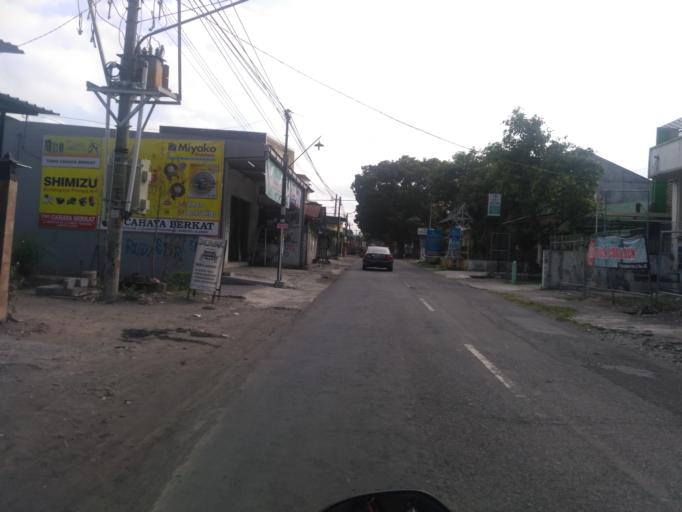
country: ID
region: Daerah Istimewa Yogyakarta
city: Yogyakarta
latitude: -7.7590
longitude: 110.3460
